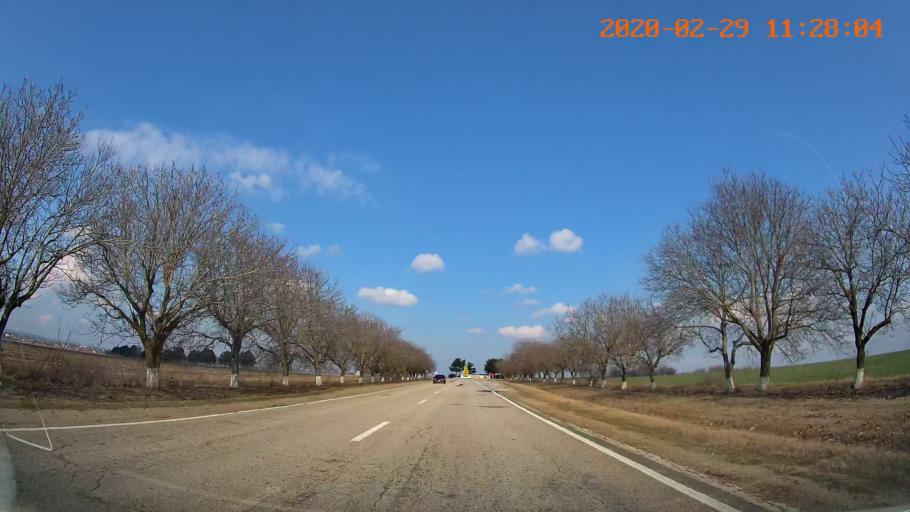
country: MD
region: Telenesti
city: Cocieri
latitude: 47.4778
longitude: 29.1399
